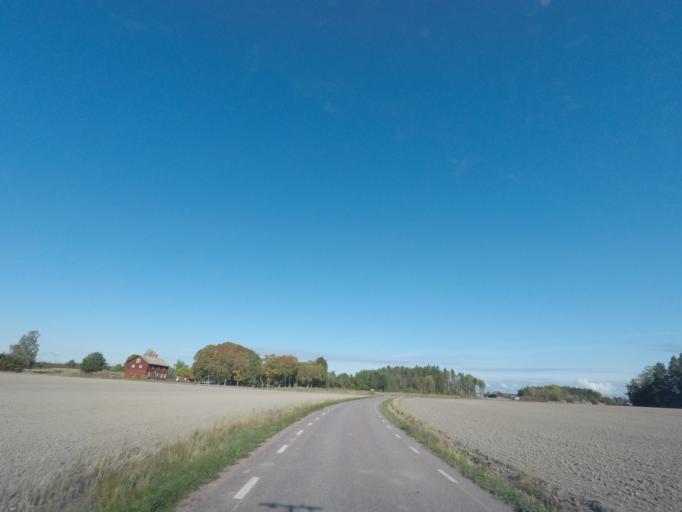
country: SE
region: Vaestmanland
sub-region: Vasteras
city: Vasteras
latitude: 59.5727
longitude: 16.4533
